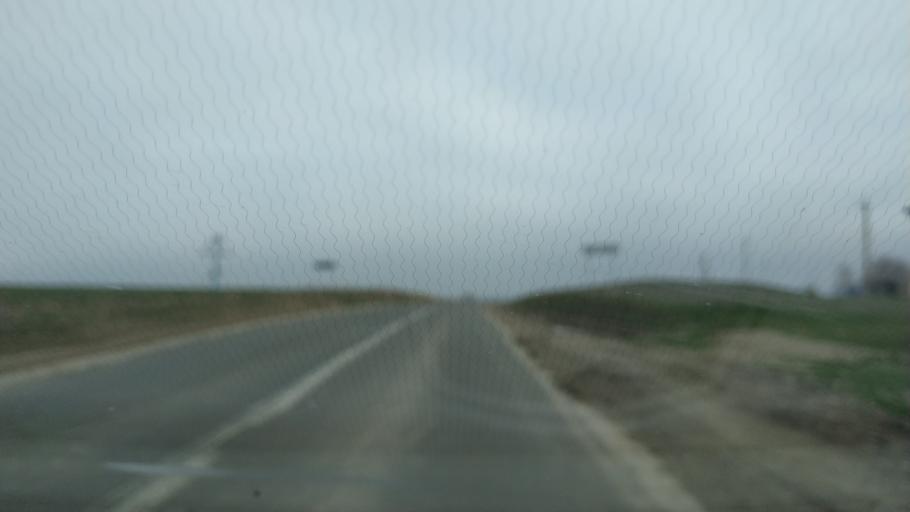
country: MD
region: Straseni
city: Taraclia
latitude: 45.9337
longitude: 28.5837
